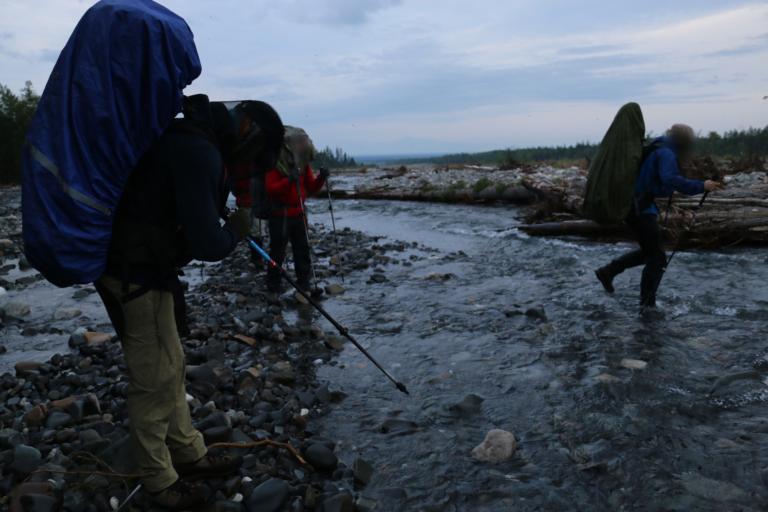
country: RU
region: Respublika Buryatiya
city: Novyy Uoyan
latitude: 56.1891
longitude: 111.5111
